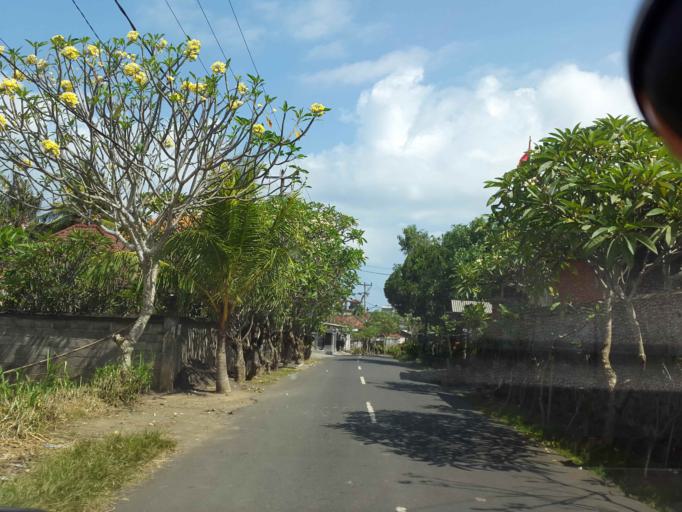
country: ID
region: Bali
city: Klungkung
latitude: -8.5492
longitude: 115.3788
